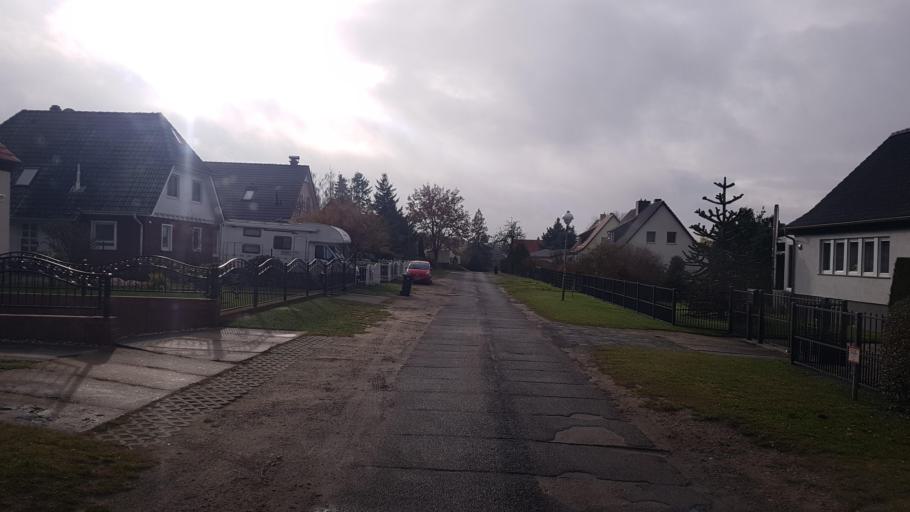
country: DE
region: Brandenburg
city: Roskow
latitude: 52.4218
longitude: 12.7194
